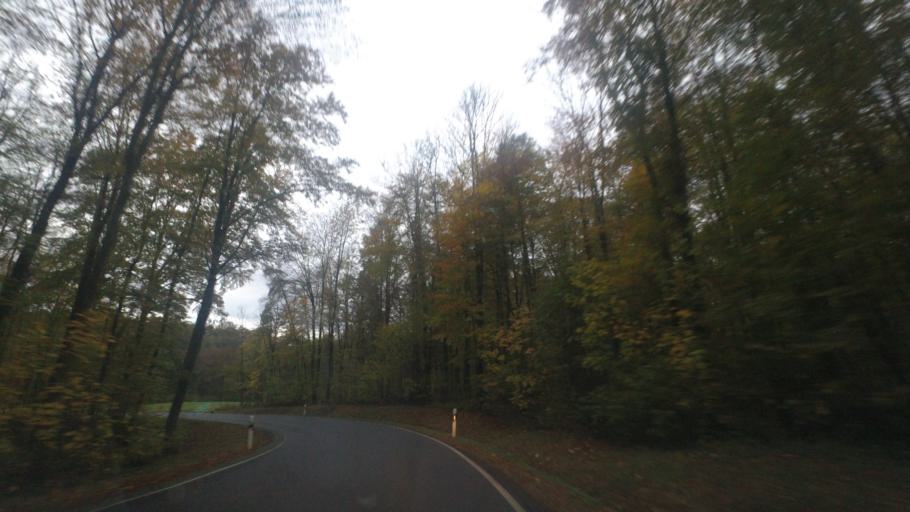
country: DE
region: Hesse
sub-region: Regierungsbezirk Darmstadt
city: Steinau an der Strasse
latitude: 50.3378
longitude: 9.4236
